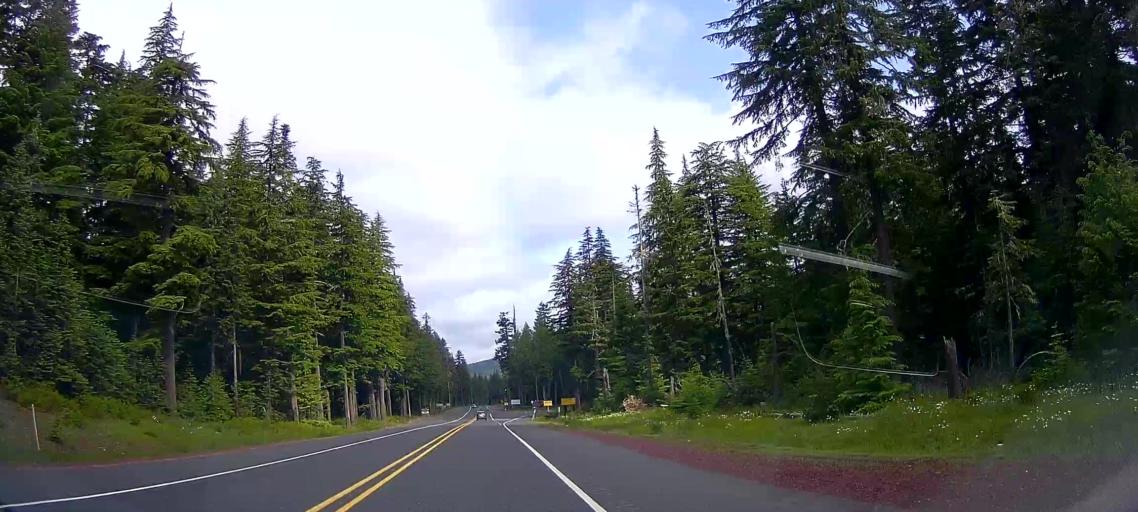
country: US
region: Oregon
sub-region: Clackamas County
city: Mount Hood Village
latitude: 45.2269
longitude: -121.6987
